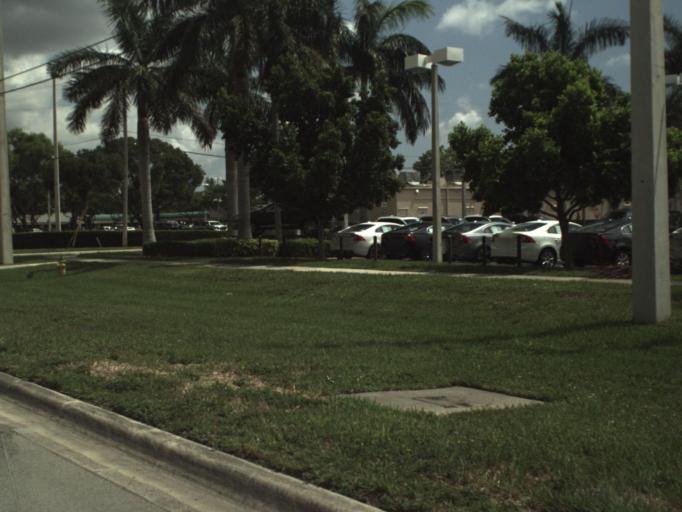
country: US
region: Florida
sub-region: Broward County
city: Margate
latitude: 26.2566
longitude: -80.2014
